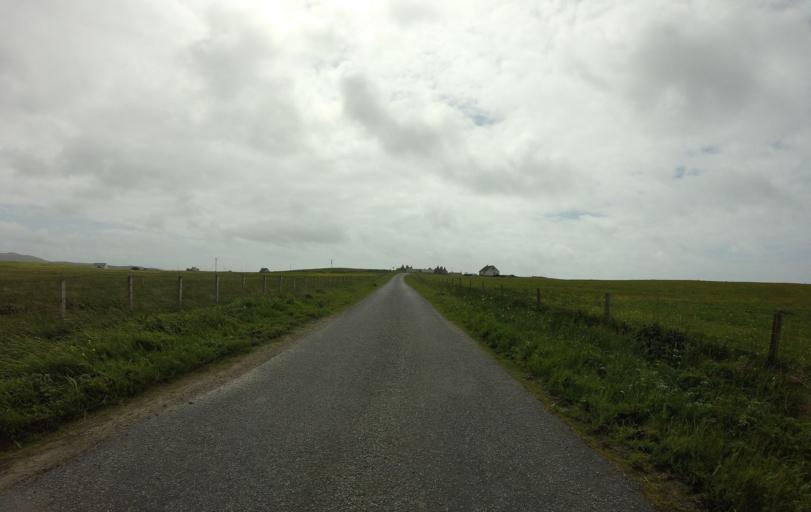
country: GB
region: Scotland
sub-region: Eilean Siar
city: Isle of South Uist
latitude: 57.2630
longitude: -7.4059
